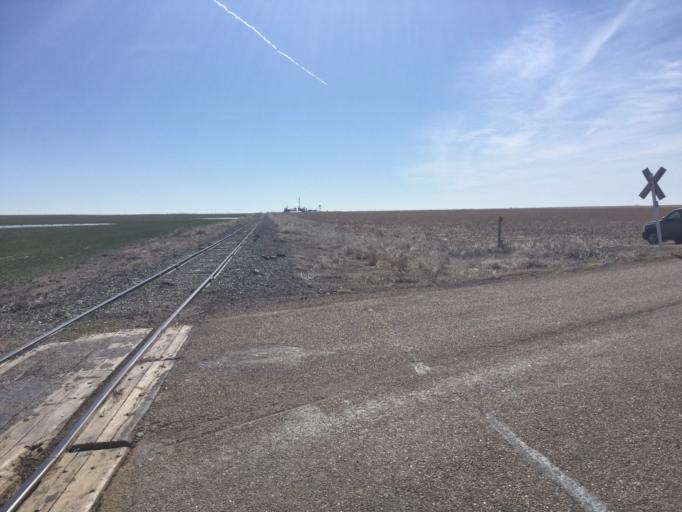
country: US
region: Kansas
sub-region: Grant County
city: Ulysses
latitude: 37.5537
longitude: -101.2174
